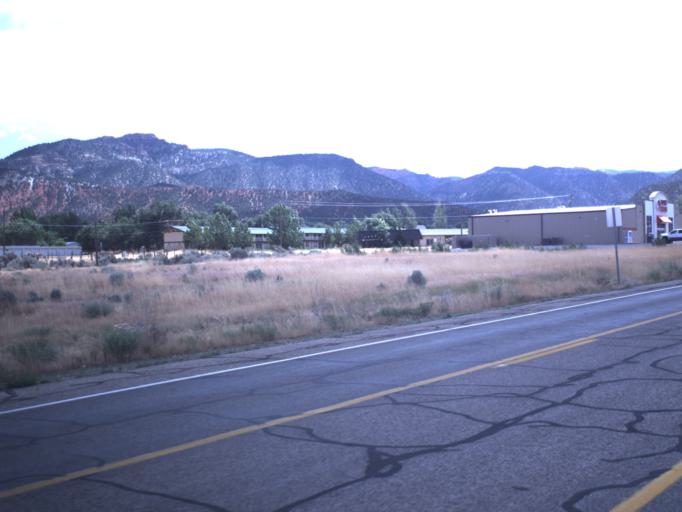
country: US
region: Utah
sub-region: Iron County
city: Parowan
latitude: 37.8530
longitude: -112.8279
